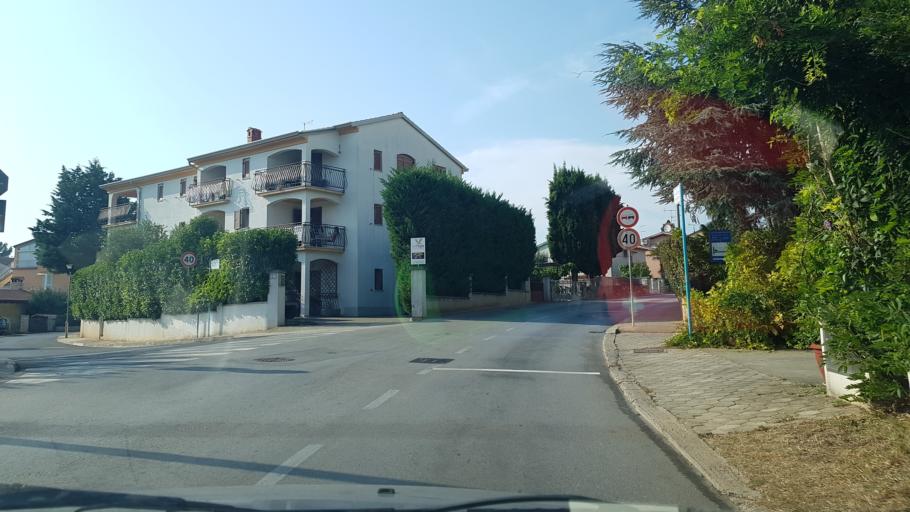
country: HR
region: Istarska
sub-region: Grad Rovinj
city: Rovinj
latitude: 45.1009
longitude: 13.6352
